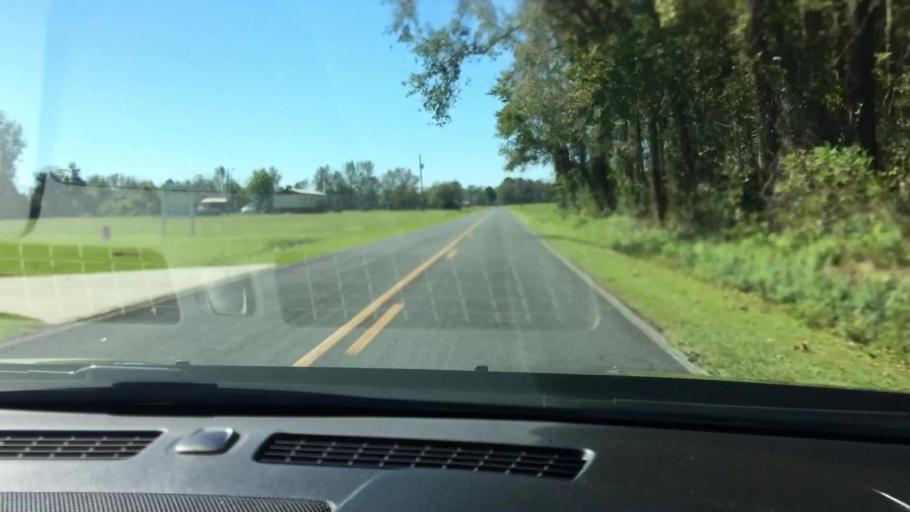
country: US
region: North Carolina
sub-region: Pitt County
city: Grifton
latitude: 35.2991
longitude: -77.3221
